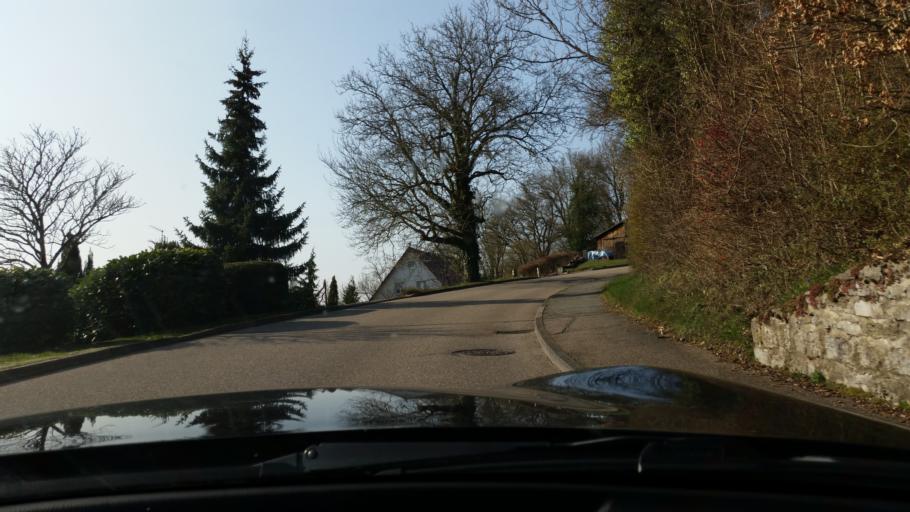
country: DE
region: Baden-Wuerttemberg
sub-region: Regierungsbezirk Stuttgart
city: Mockmuhl
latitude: 49.3265
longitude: 9.3597
